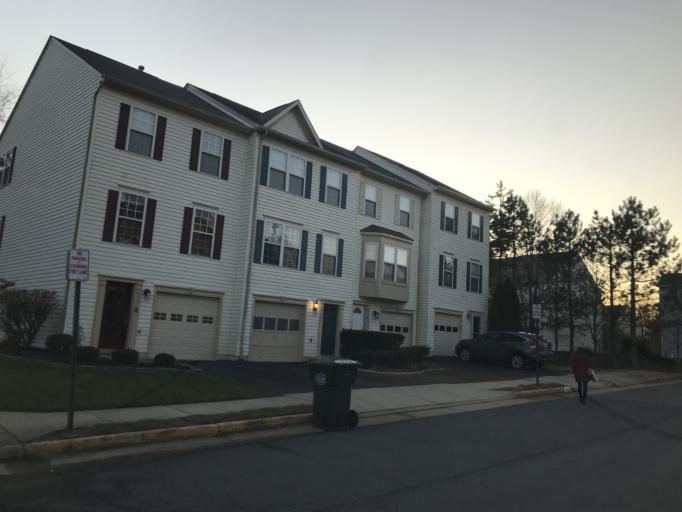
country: US
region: Virginia
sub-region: Fairfax County
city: Franconia
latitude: 38.7812
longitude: -77.1576
